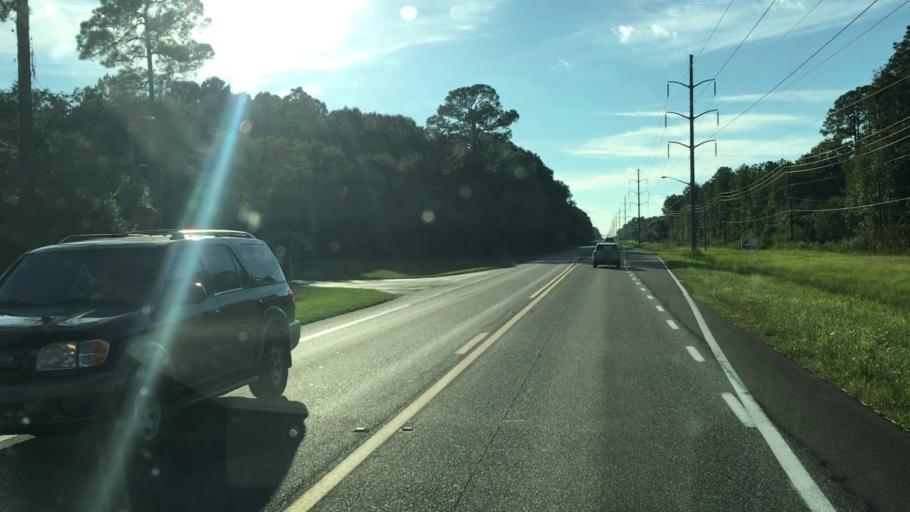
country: US
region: Florida
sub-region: Alachua County
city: Gainesville
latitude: 29.7032
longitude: -82.3314
